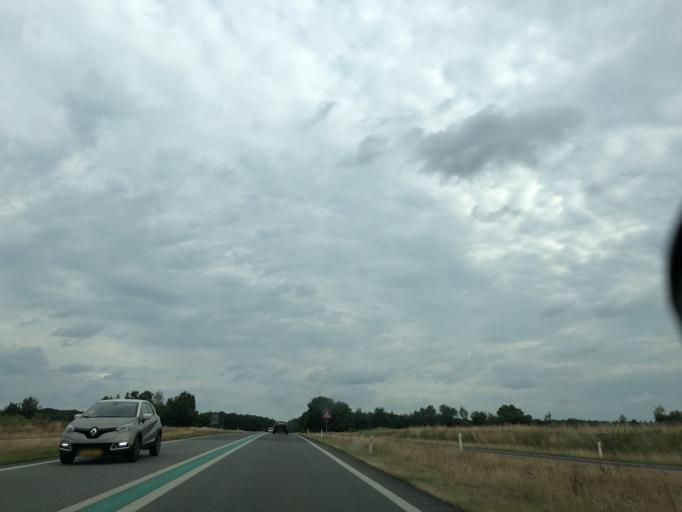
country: NL
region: Drenthe
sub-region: Gemeente Borger-Odoorn
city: Borger
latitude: 52.9731
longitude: 6.7767
